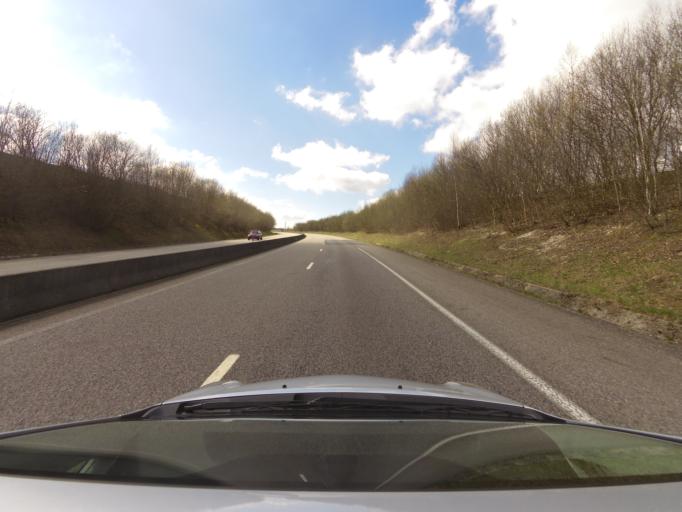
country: FR
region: Haute-Normandie
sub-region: Departement de la Seine-Maritime
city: Foucarmont
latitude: 49.8380
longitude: 1.5319
